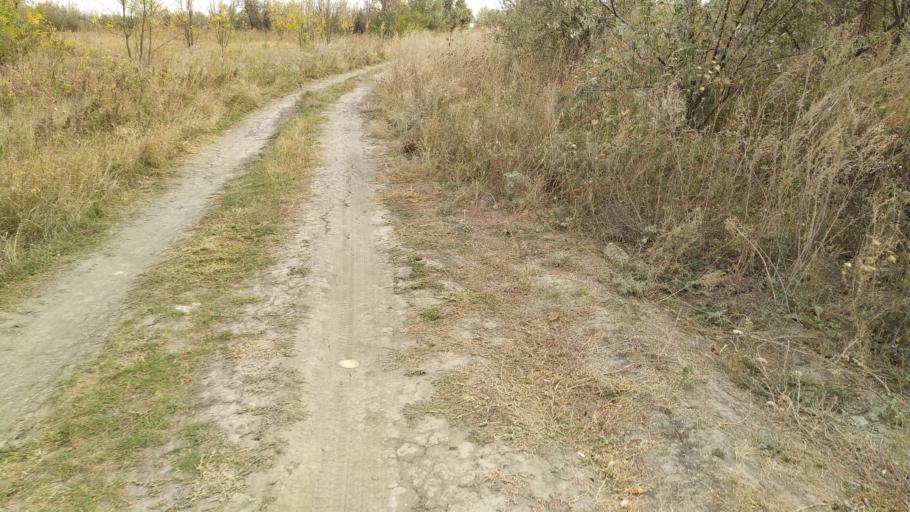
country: RU
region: Rostov
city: Kuleshovka
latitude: 47.1370
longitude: 39.5805
